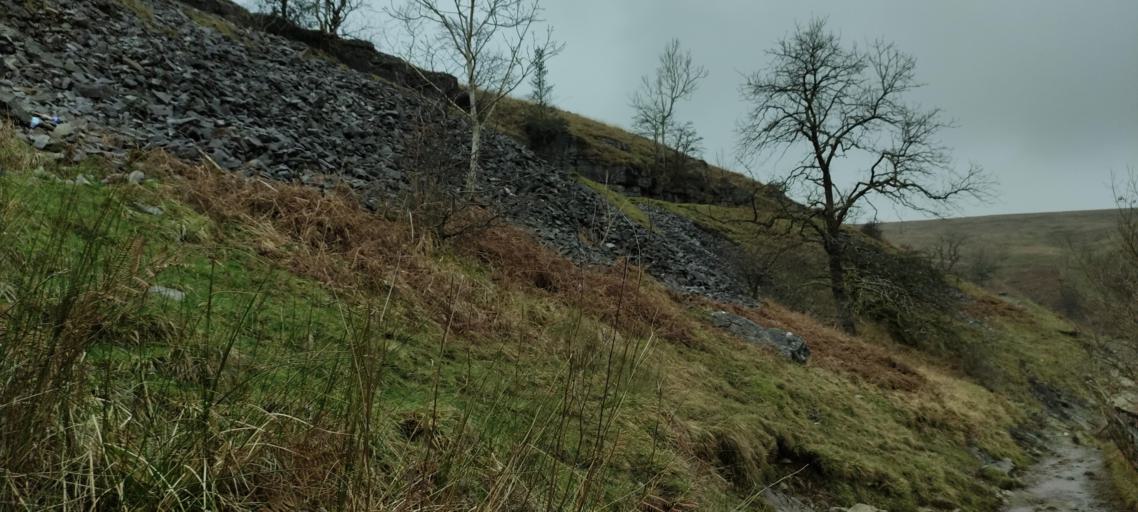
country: GB
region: England
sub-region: North Yorkshire
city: Ingleton
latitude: 54.1705
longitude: -2.4693
